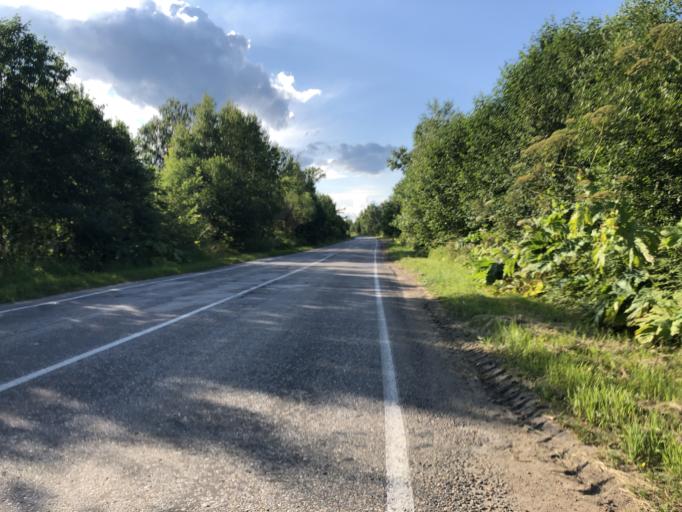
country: RU
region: Tverskaya
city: Rzhev
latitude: 56.2709
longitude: 34.2469
